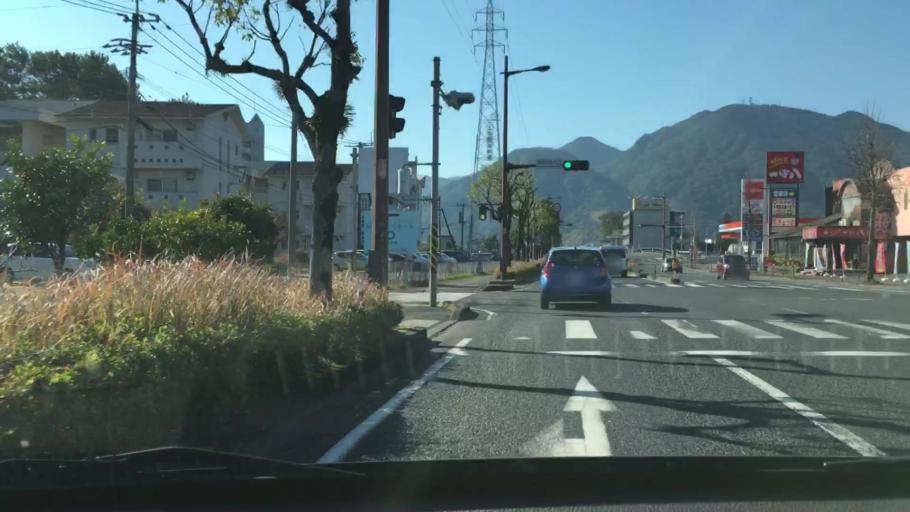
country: JP
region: Kagoshima
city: Kajiki
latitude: 31.7183
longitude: 130.6201
